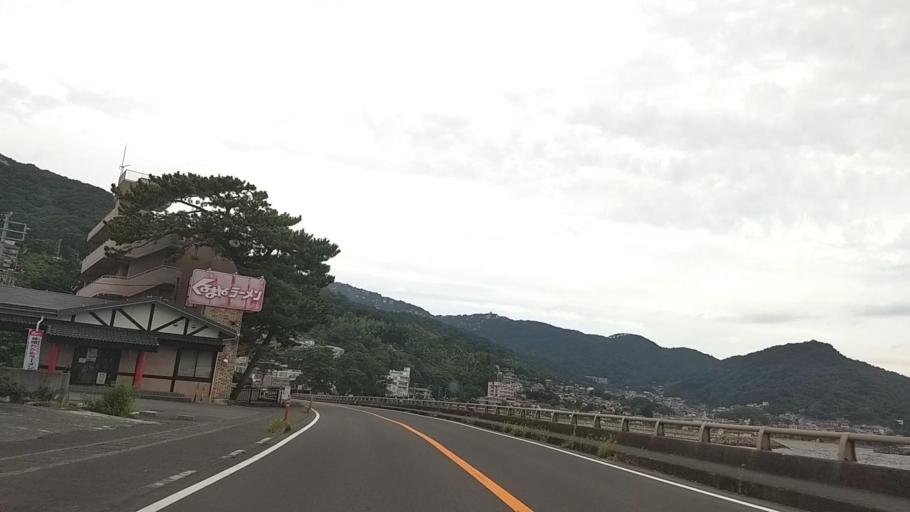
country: JP
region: Shizuoka
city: Atami
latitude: 35.0513
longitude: 139.0707
